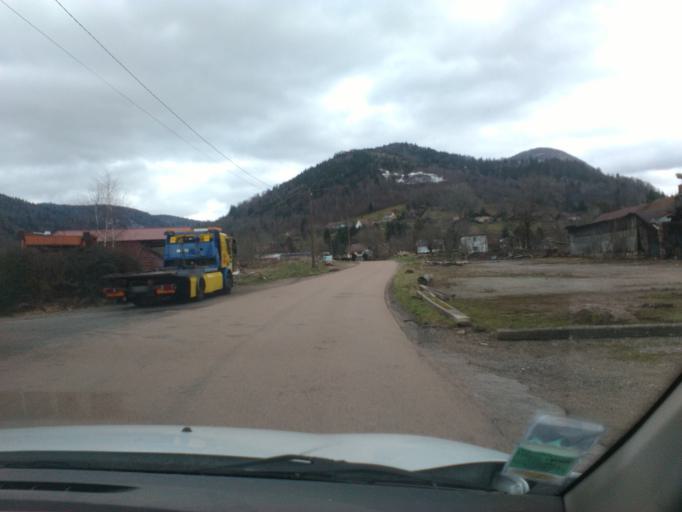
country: FR
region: Lorraine
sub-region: Departement des Vosges
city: Bussang
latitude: 47.8908
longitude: 6.8659
